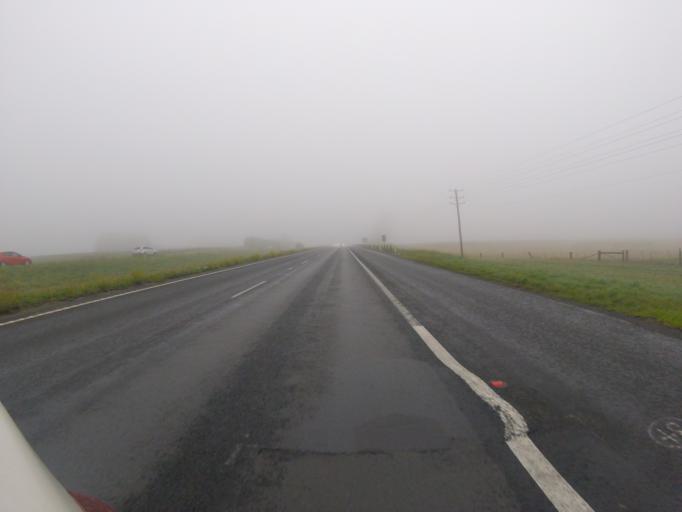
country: AU
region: Victoria
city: Brown Hill
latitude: -37.5587
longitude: 143.9550
